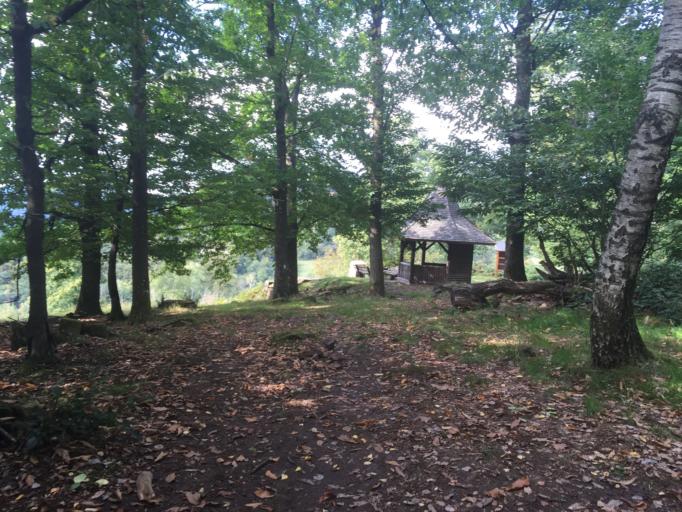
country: DE
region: Baden-Wuerttemberg
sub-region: Karlsruhe Region
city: Eberbach
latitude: 49.4511
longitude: 9.0067
